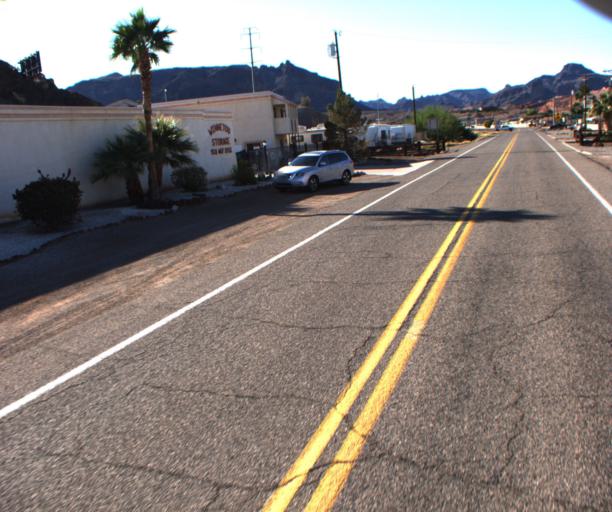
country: US
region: Arizona
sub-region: La Paz County
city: Cienega Springs
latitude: 34.2869
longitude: -114.1356
